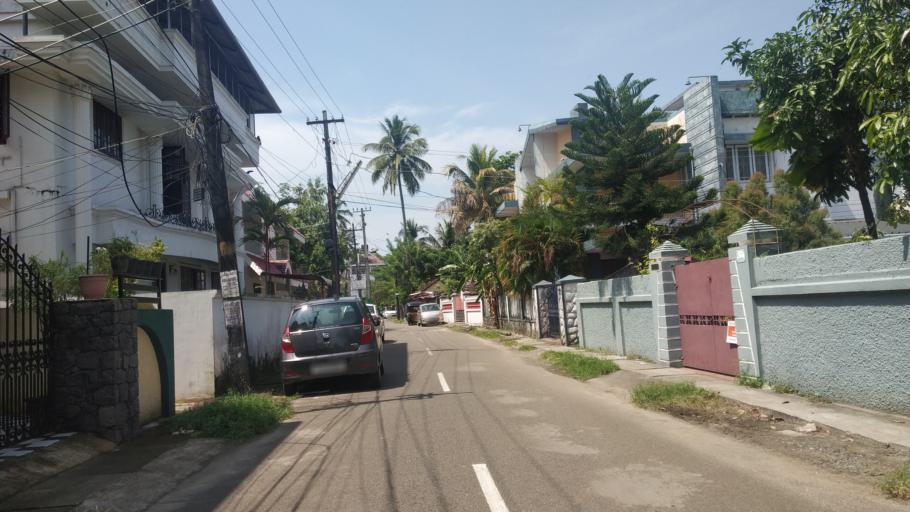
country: IN
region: Kerala
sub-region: Ernakulam
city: Cochin
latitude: 9.9593
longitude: 76.2418
